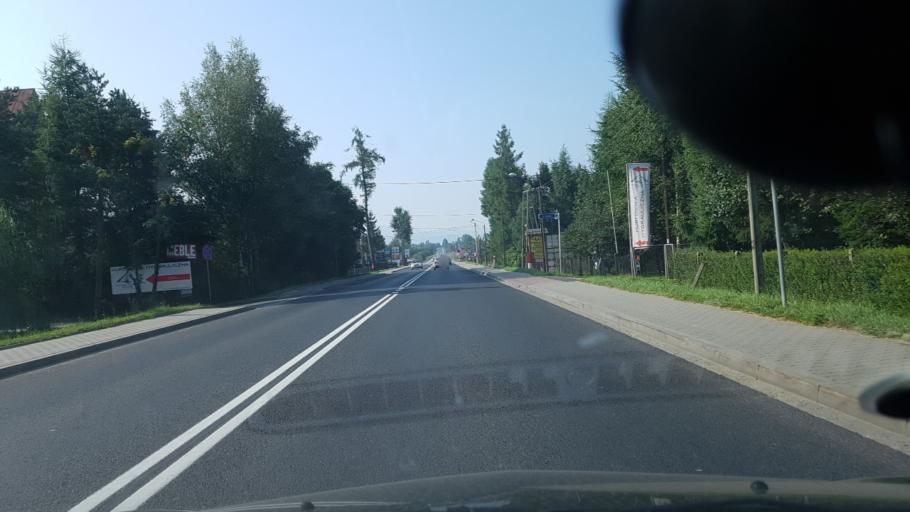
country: PL
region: Lesser Poland Voivodeship
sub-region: Powiat nowotarski
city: Jablonka
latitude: 49.4739
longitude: 19.6929
